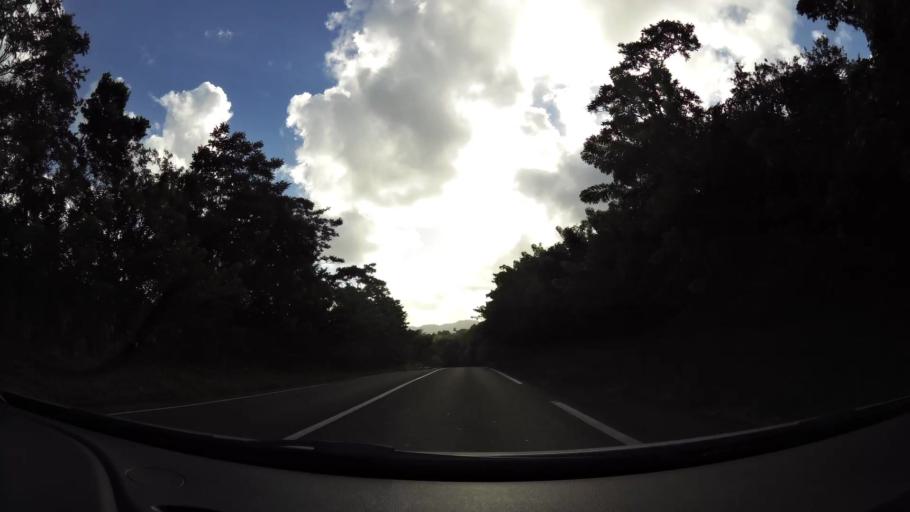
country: MQ
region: Martinique
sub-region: Martinique
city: Ducos
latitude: 14.6000
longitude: -60.9483
